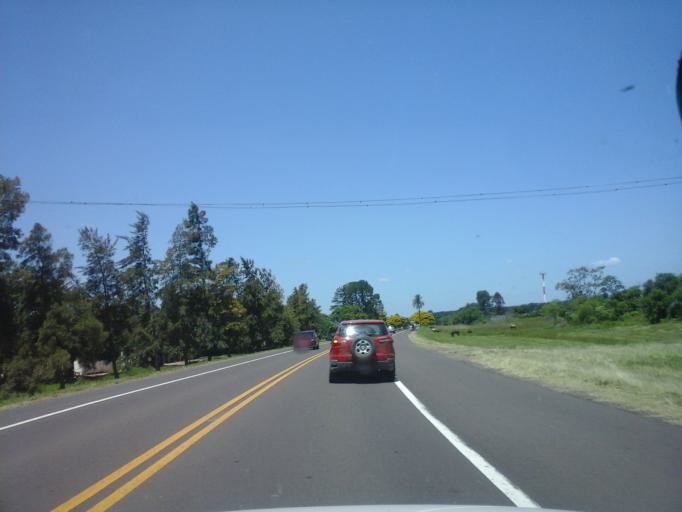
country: AR
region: Corrientes
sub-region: Departamento de San Cosme
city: San Cosme
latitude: -27.3775
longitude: -58.5092
